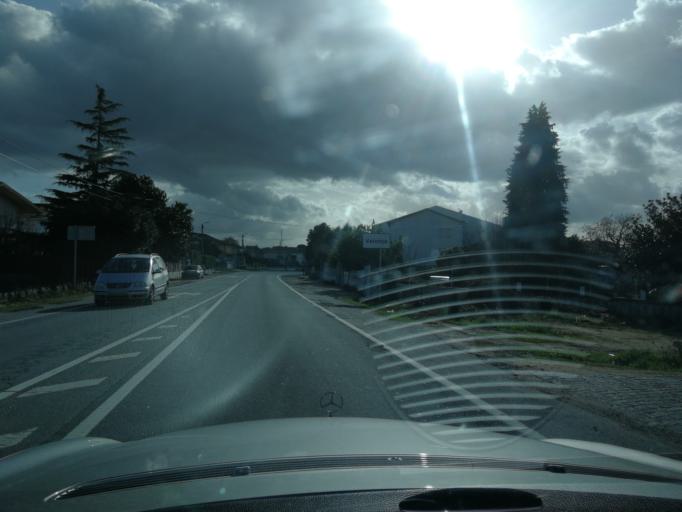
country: PT
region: Viana do Castelo
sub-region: Valenca
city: Valenza
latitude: 42.0324
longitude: -8.6297
